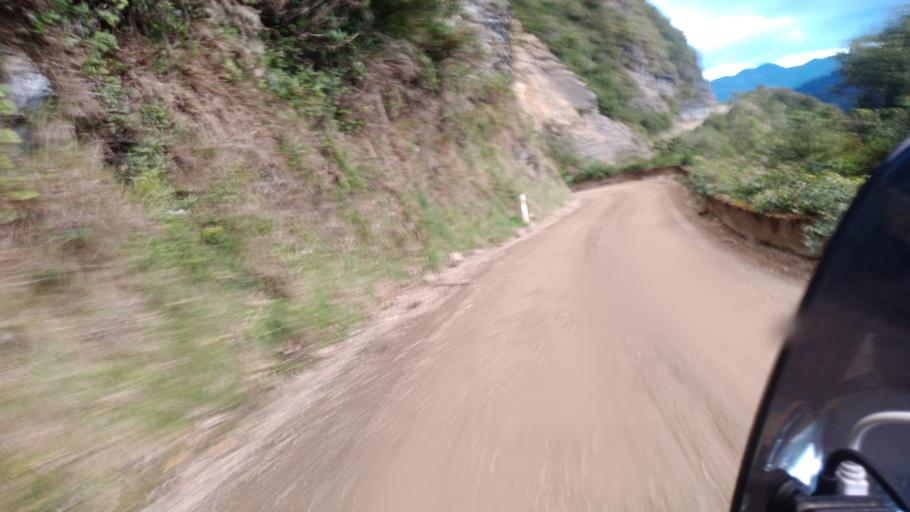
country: NZ
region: Hawke's Bay
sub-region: Wairoa District
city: Wairoa
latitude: -38.7291
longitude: 177.0661
